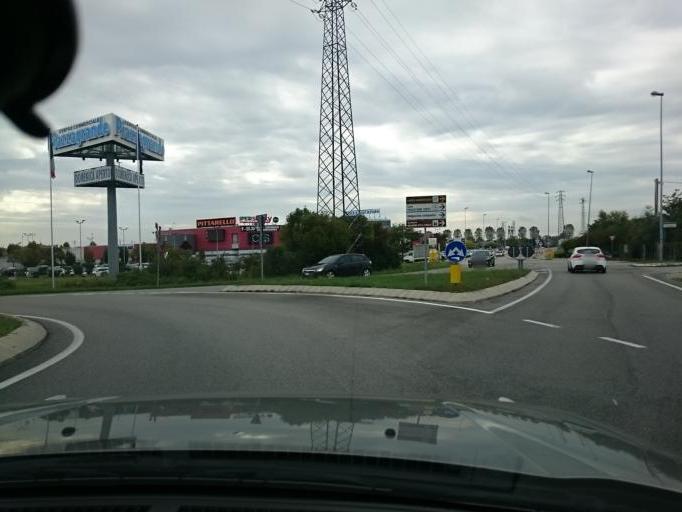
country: IT
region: Veneto
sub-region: Provincia di Padova
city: Sant'Angelo di Piove di Sacco
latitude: 45.3065
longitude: 12.0207
